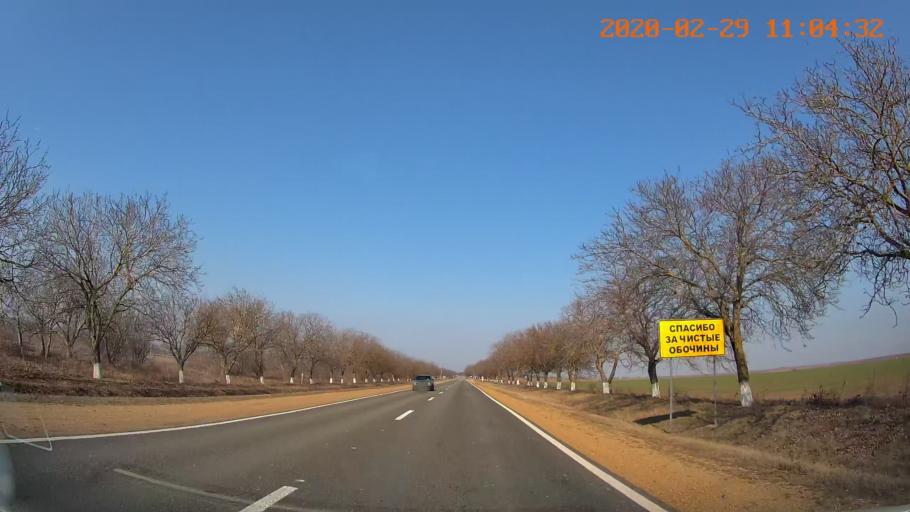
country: MD
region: Criuleni
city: Criuleni
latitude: 47.1905
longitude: 29.2011
